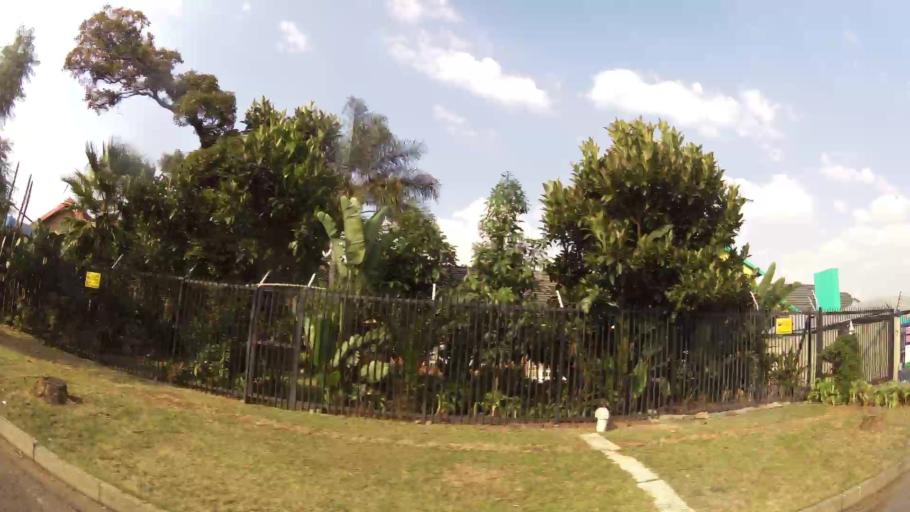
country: ZA
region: Gauteng
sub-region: Ekurhuleni Metropolitan Municipality
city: Boksburg
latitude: -26.2305
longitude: 28.2490
